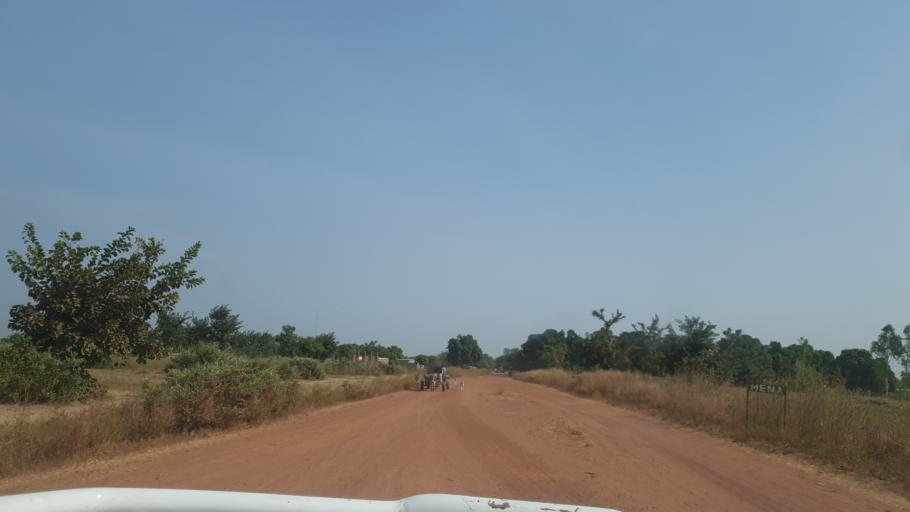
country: ML
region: Koulikoro
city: Dioila
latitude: 12.2218
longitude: -6.2117
